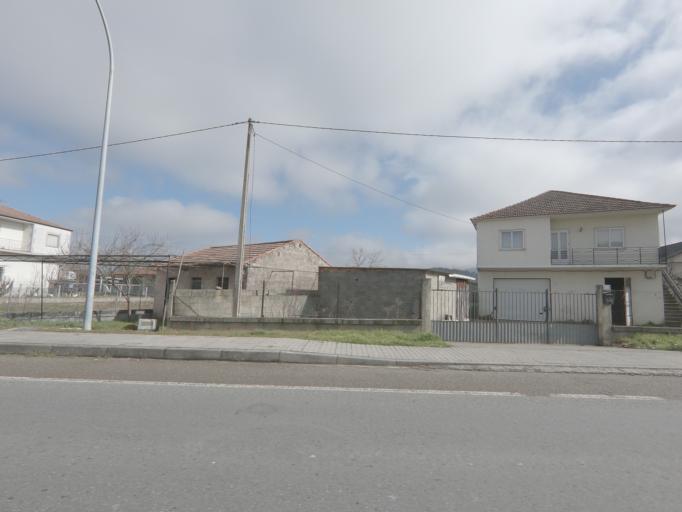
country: ES
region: Galicia
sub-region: Provincia de Ourense
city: Verin
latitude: 41.9176
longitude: -7.4435
